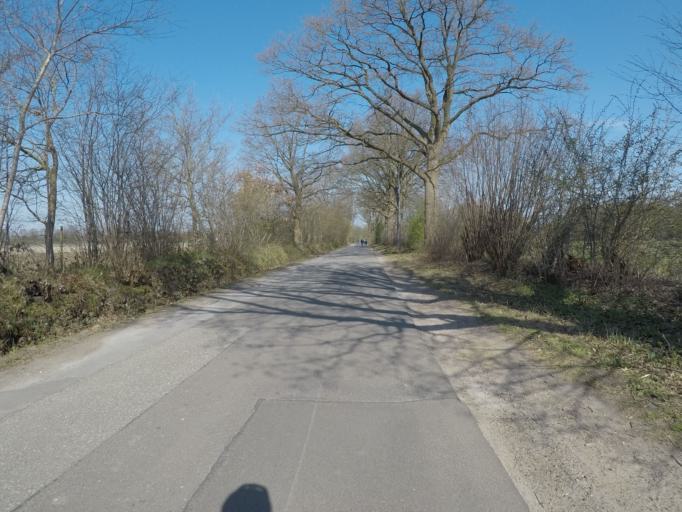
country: DE
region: Schleswig-Holstein
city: Halstenbek
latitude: 53.5924
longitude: 9.8170
